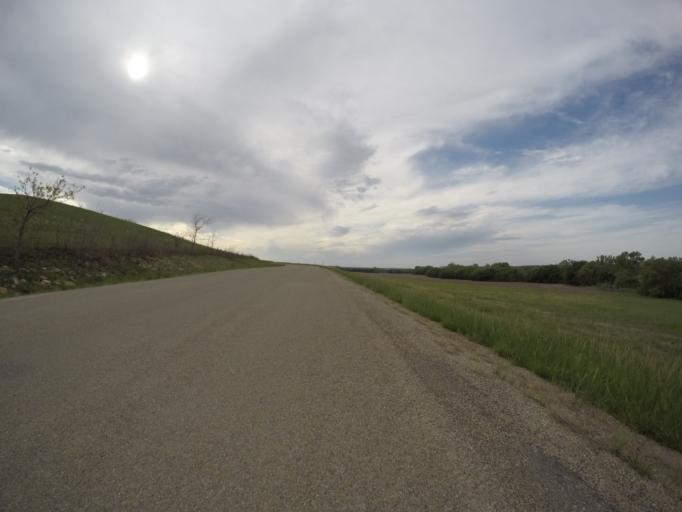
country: US
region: Kansas
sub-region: Riley County
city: Ogden
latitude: 39.0300
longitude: -96.6138
